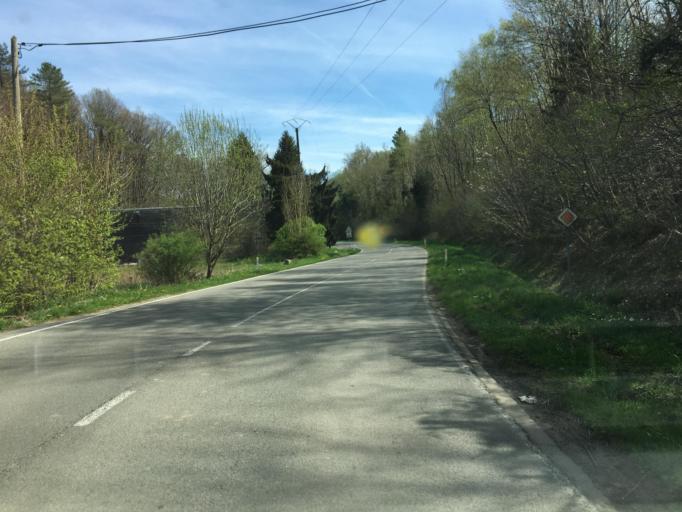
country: BE
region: Wallonia
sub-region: Province de Liege
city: Aywaille
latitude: 50.4199
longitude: 5.6750
